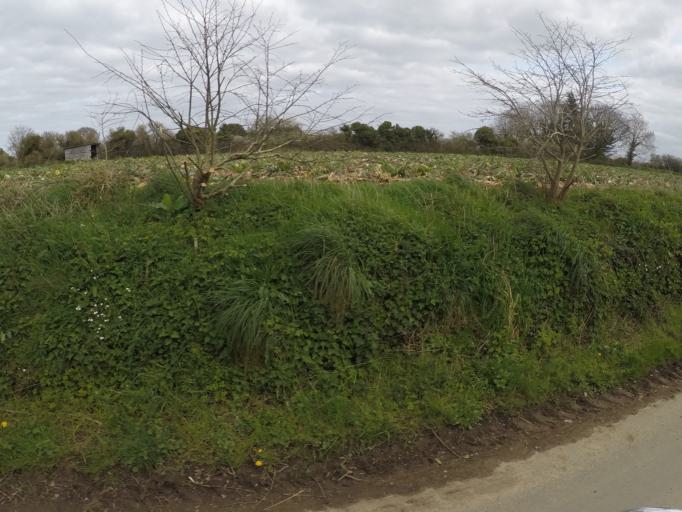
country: FR
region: Brittany
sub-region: Departement des Cotes-d'Armor
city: Plouha
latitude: 48.7105
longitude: -2.9392
